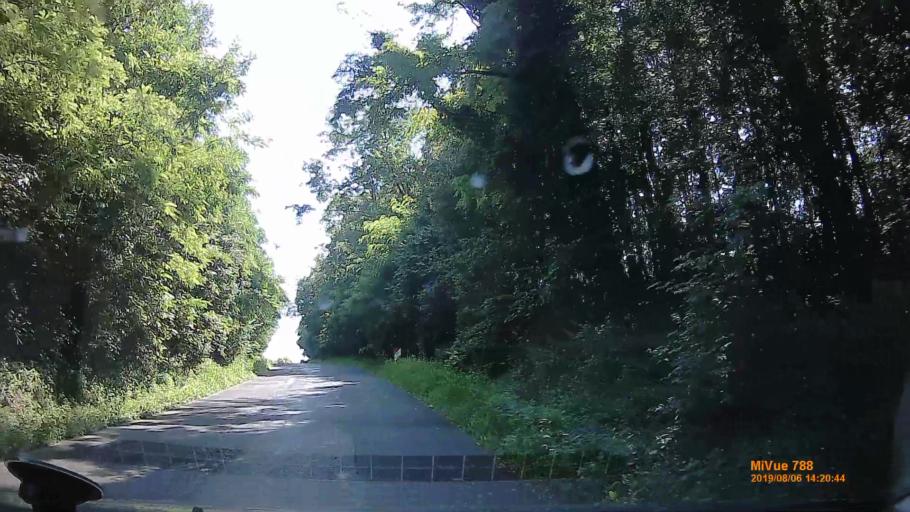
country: HU
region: Zala
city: Zalakomar
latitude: 46.5222
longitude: 17.0870
